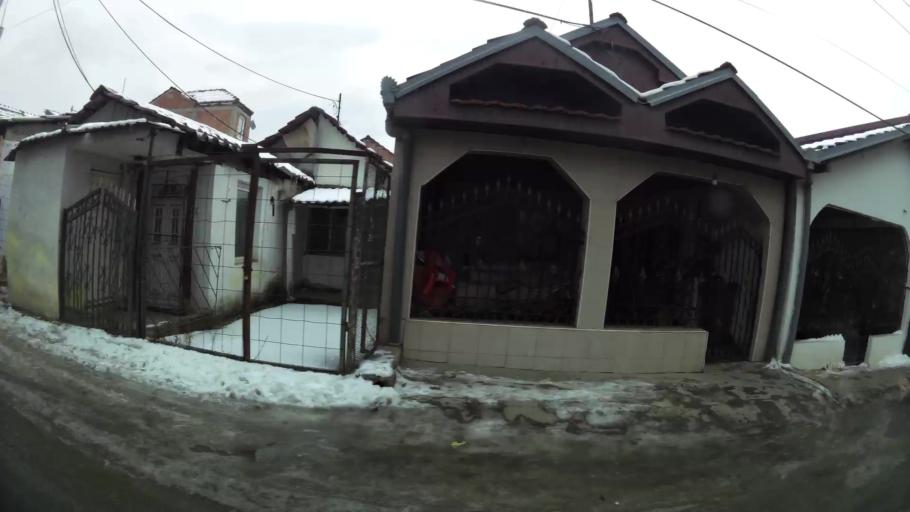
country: MK
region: Suto Orizari
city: Suto Orizare
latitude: 42.0455
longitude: 21.4256
